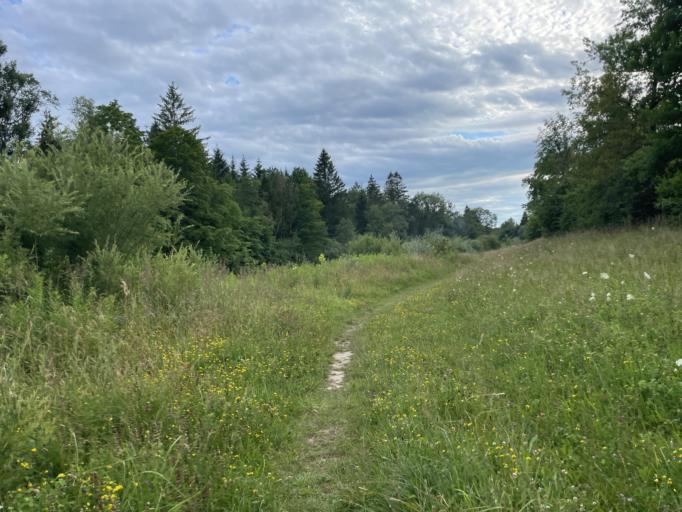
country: DE
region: Bavaria
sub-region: Upper Bavaria
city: Peissenberg
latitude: 47.7801
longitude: 11.0647
